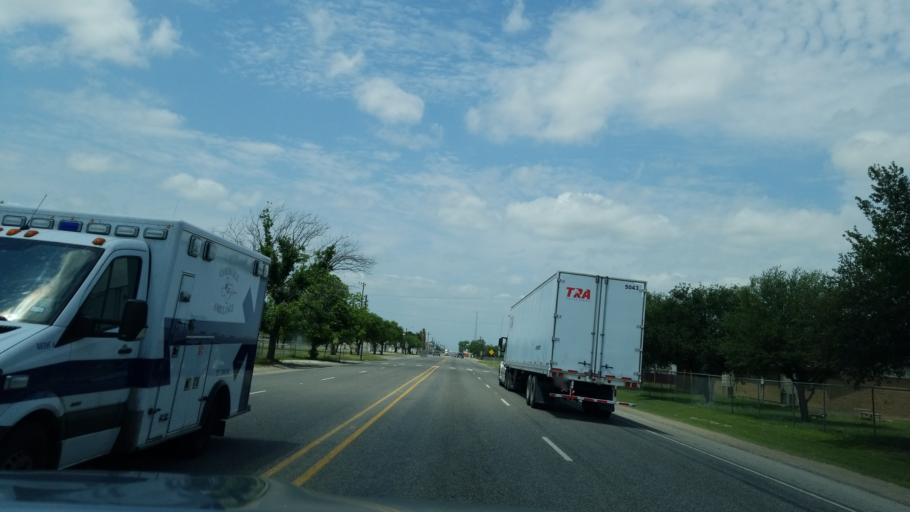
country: US
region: Texas
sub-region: Zavala County
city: La Pryor
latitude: 28.9442
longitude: -99.8413
